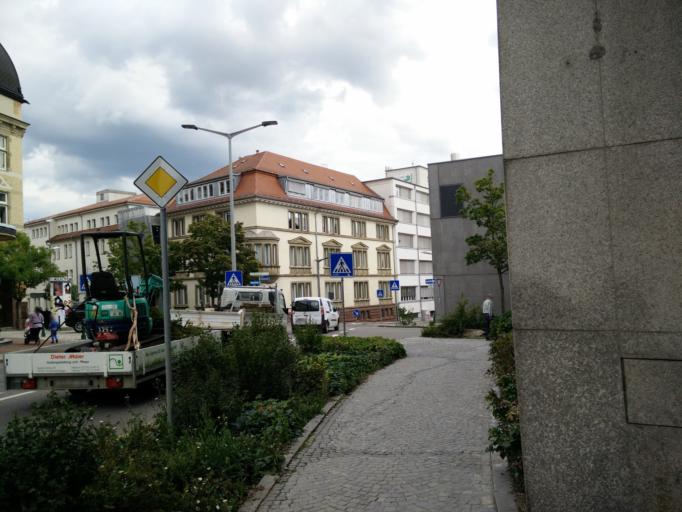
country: DE
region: Baden-Wuerttemberg
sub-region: Freiburg Region
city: Dauchingen
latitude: 48.0614
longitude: 8.5339
